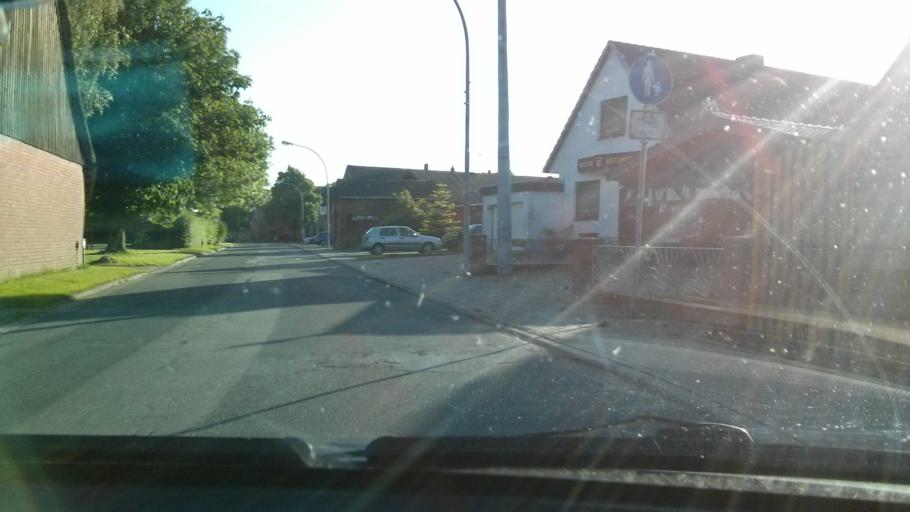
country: DE
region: Lower Saxony
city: Nordenham
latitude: 53.4785
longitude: 8.5521
